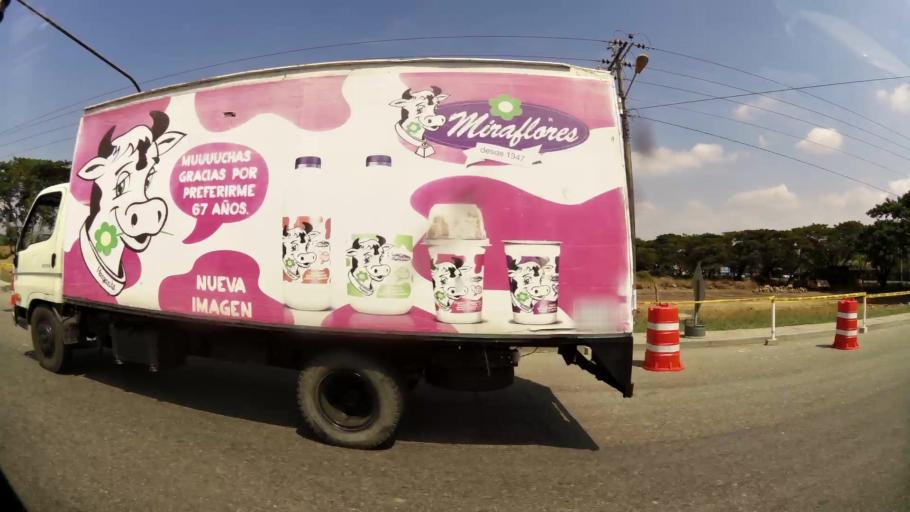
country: EC
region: Guayas
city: Eloy Alfaro
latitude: -2.1233
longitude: -79.8648
